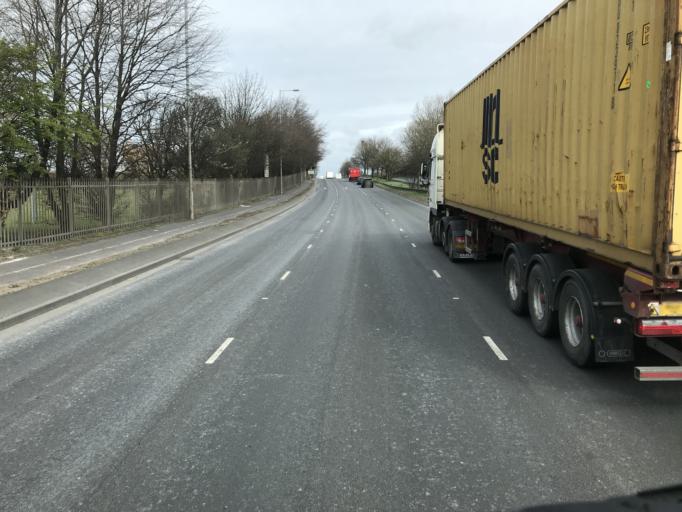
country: GB
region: England
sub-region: Sefton
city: Maghull
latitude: 53.4853
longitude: -2.9605
